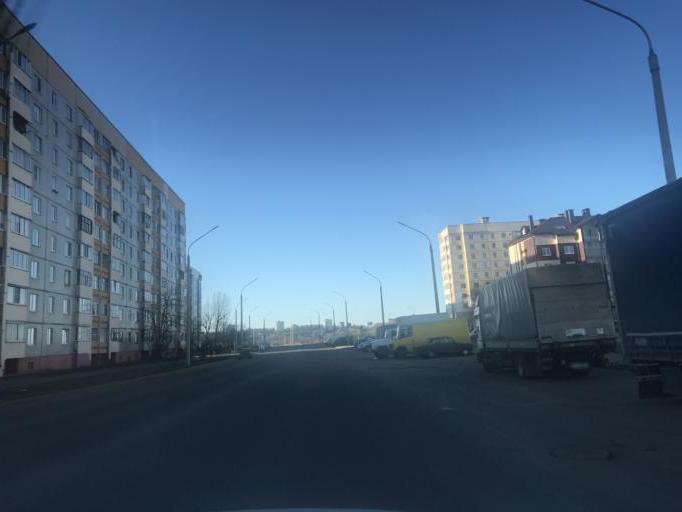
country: BY
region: Mogilev
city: Mahilyow
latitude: 53.8828
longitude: 30.3764
